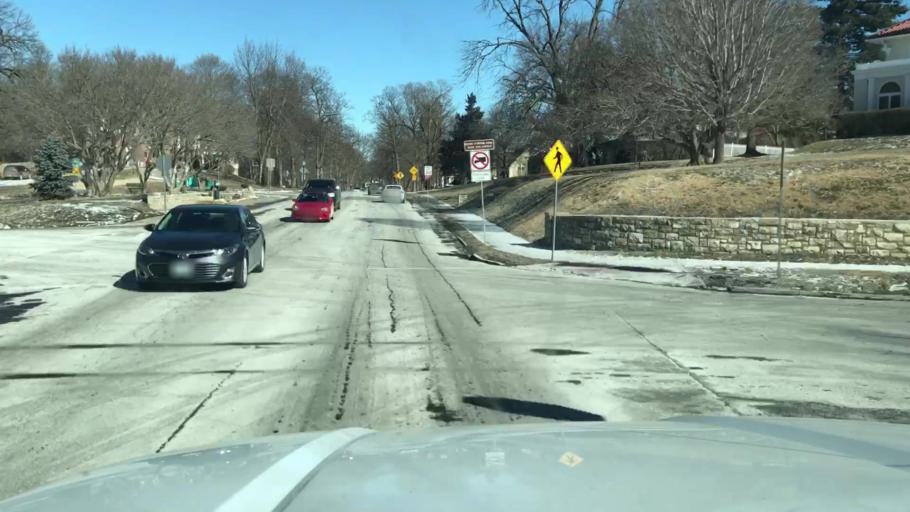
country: US
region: Missouri
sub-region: Buchanan County
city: Saint Joseph
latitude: 39.7803
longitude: -94.8254
